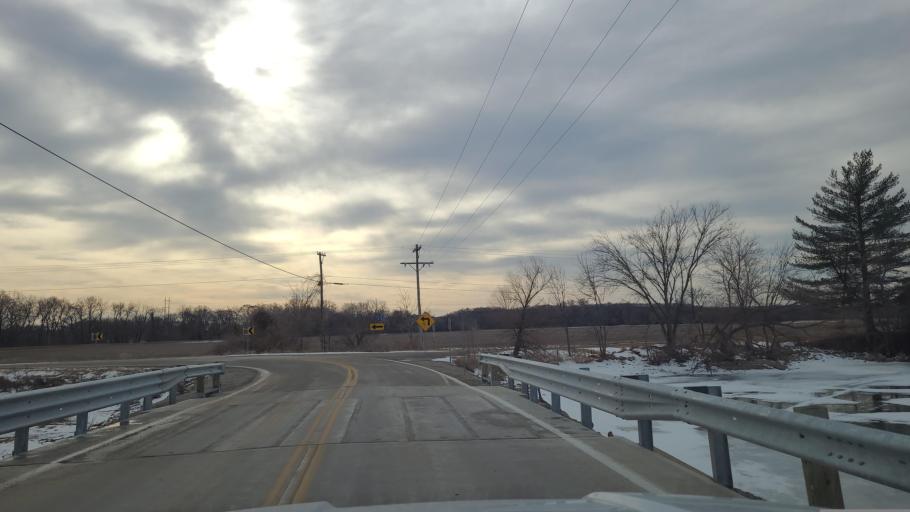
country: US
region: Kansas
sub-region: Douglas County
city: Lawrence
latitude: 39.0113
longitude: -95.2929
